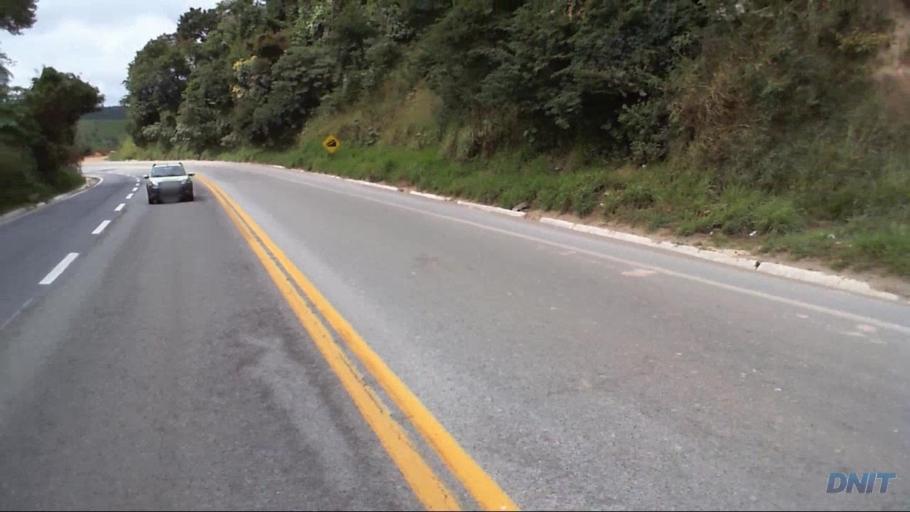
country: BR
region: Minas Gerais
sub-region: Caete
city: Caete
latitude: -19.7571
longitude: -43.6327
